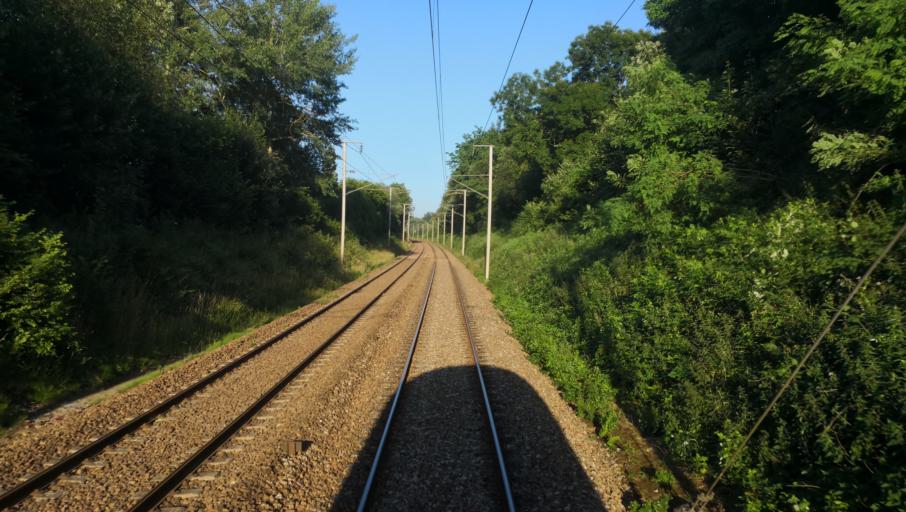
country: FR
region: Lower Normandy
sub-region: Departement du Calvados
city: Beuvillers
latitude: 49.1245
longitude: 0.2964
